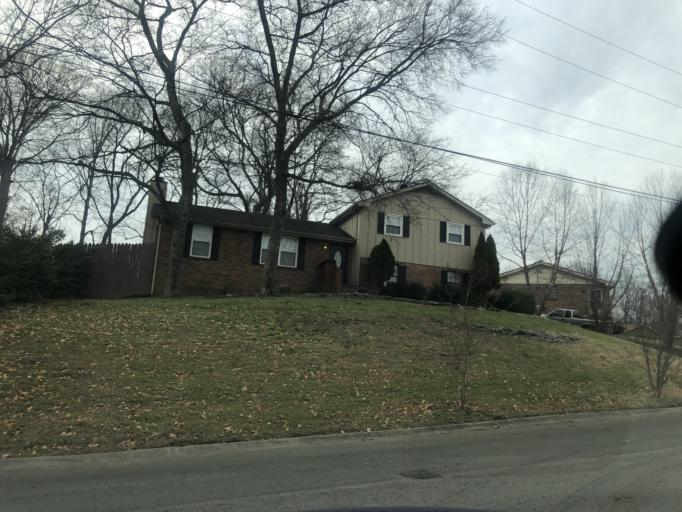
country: US
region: Tennessee
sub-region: Davidson County
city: Oak Hill
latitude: 36.0959
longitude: -86.7175
